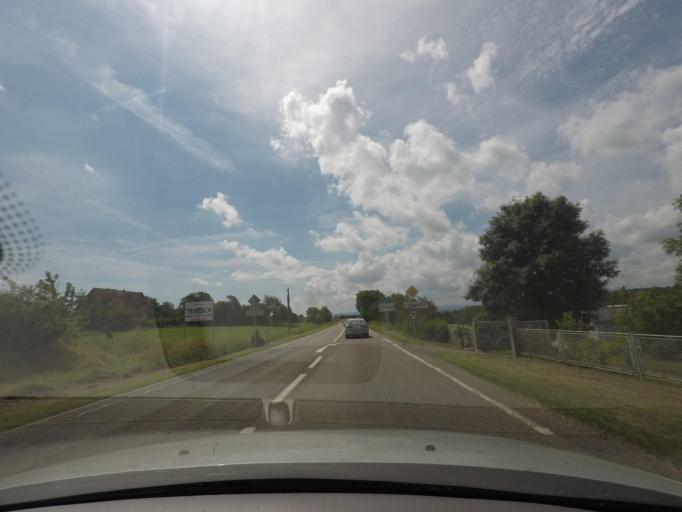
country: FR
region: Alsace
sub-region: Departement du Bas-Rhin
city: Drulingen
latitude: 48.8419
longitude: 7.2090
